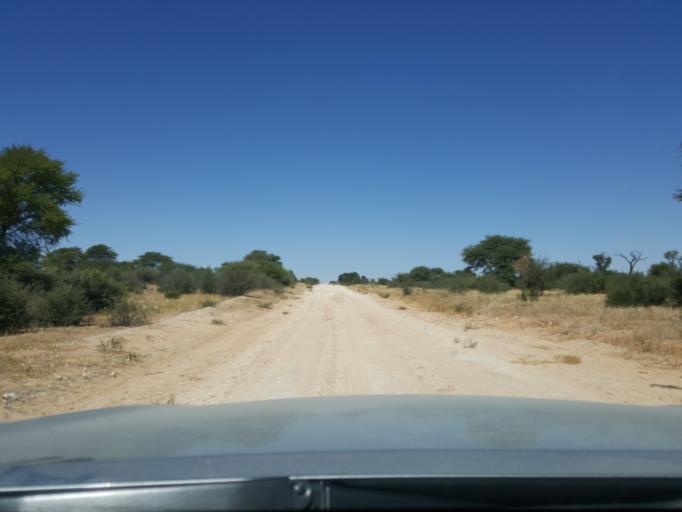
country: BW
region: Kgalagadi
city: Hukuntsi
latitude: -24.0067
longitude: 21.2132
